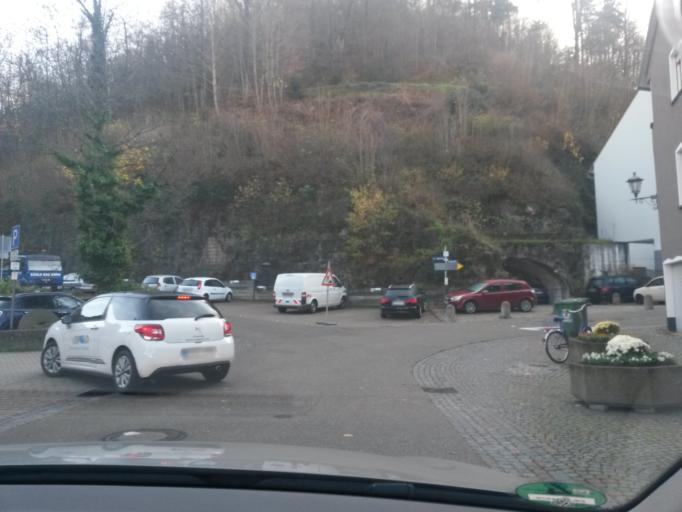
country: DE
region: Baden-Wuerttemberg
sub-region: Freiburg Region
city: Wolfach
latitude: 48.2994
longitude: 8.2245
